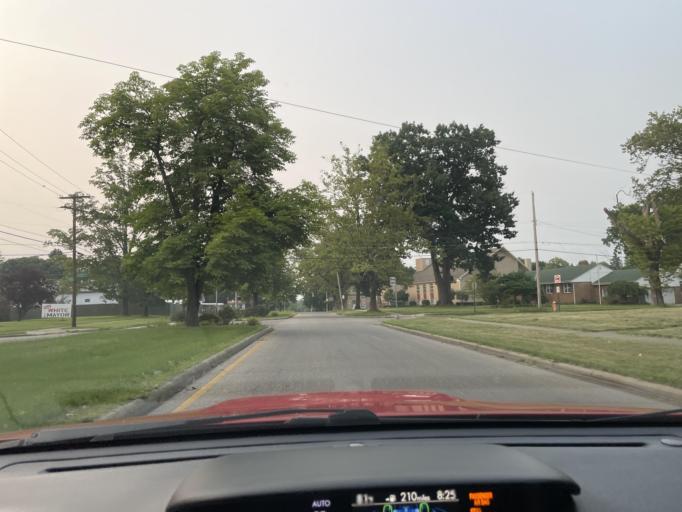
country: US
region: Ohio
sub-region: Mahoning County
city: Struthers
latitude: 41.0593
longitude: -80.6212
